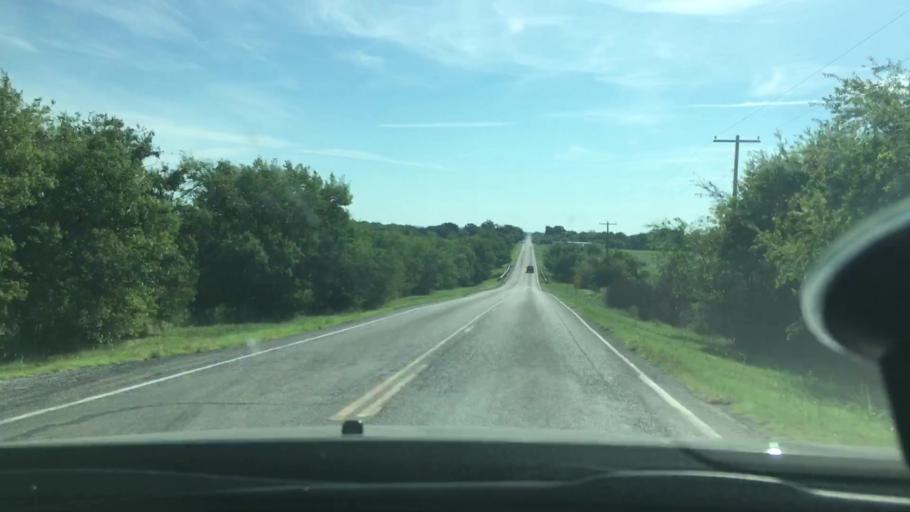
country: US
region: Oklahoma
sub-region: Carter County
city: Lone Grove
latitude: 34.3327
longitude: -97.2129
